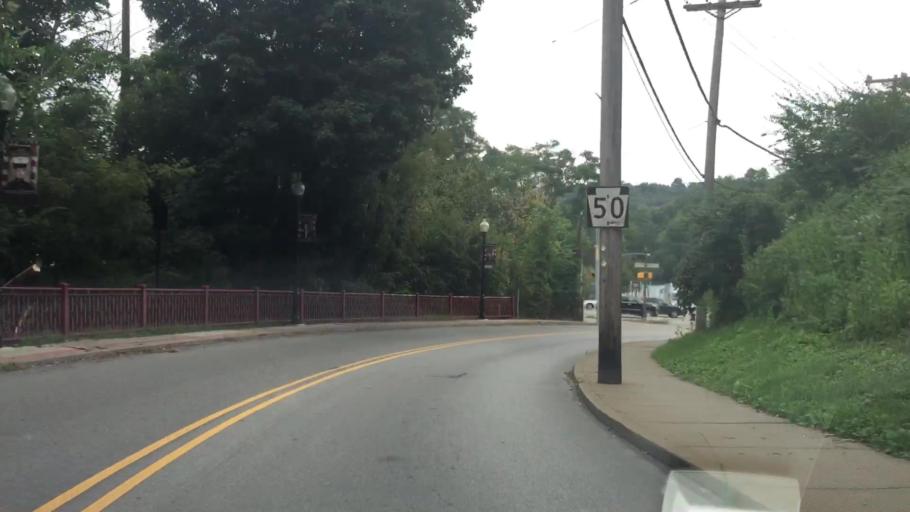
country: US
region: Pennsylvania
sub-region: Allegheny County
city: Heidelberg
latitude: 40.3963
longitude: -80.0874
